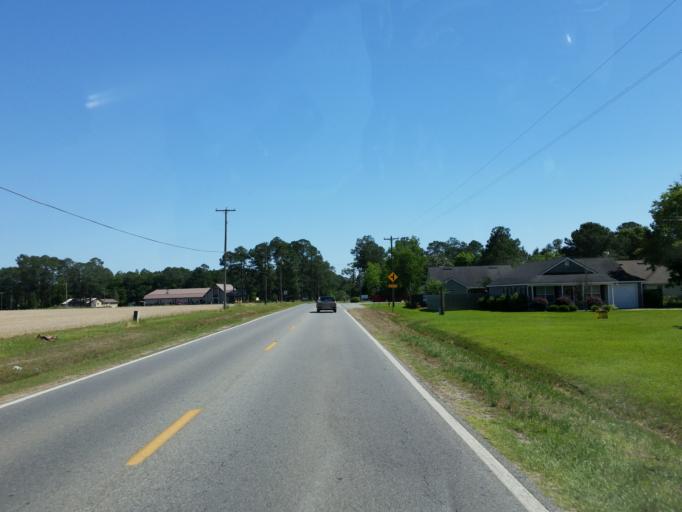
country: US
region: Georgia
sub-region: Cook County
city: Adel
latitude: 31.1175
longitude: -83.4150
